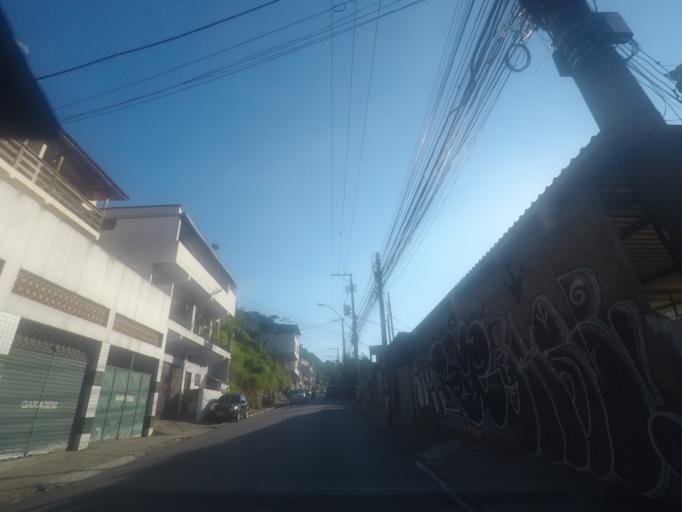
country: BR
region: Rio de Janeiro
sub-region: Petropolis
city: Petropolis
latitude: -22.4925
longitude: -43.1576
